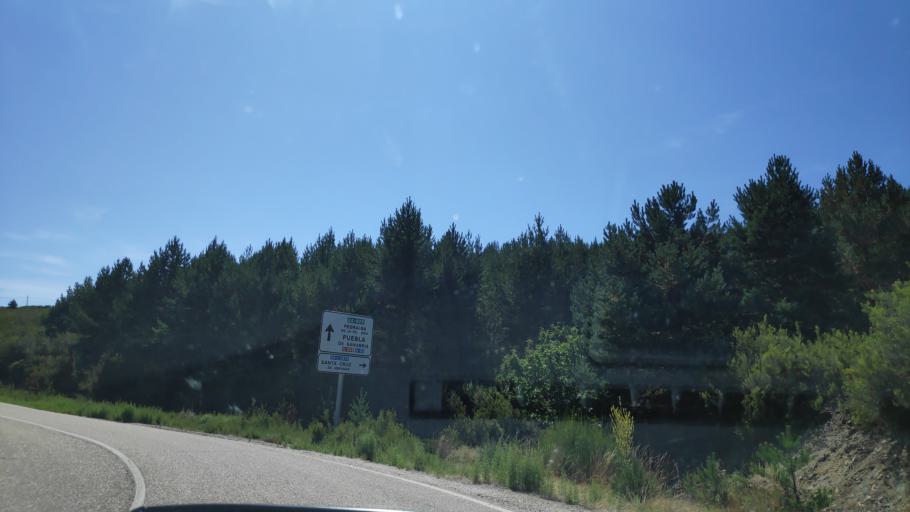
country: ES
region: Castille and Leon
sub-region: Provincia de Zamora
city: Requejo
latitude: 41.9982
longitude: -6.6921
